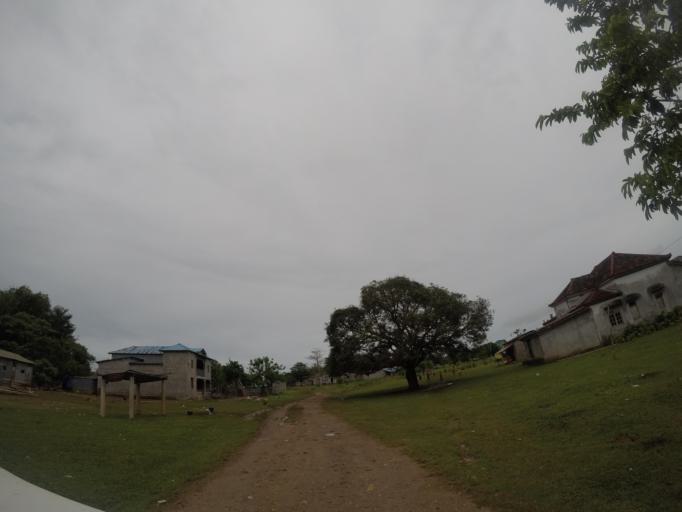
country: TL
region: Lautem
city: Lospalos
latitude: -8.5229
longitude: 127.0076
